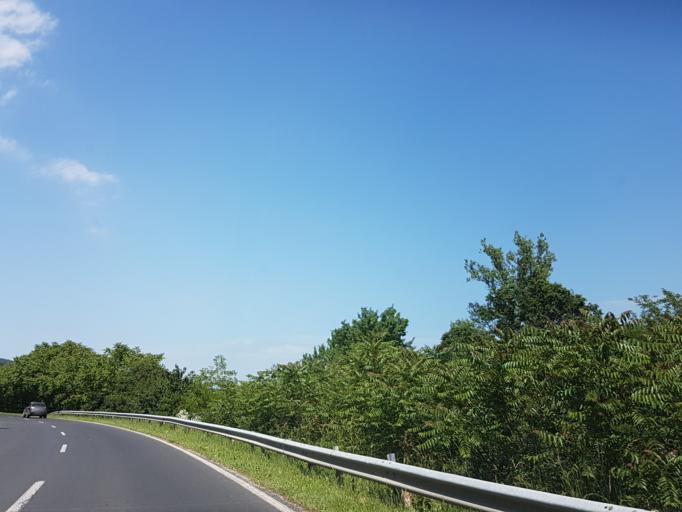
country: HU
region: Veszprem
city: Revfueloep
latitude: 46.8318
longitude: 17.6460
